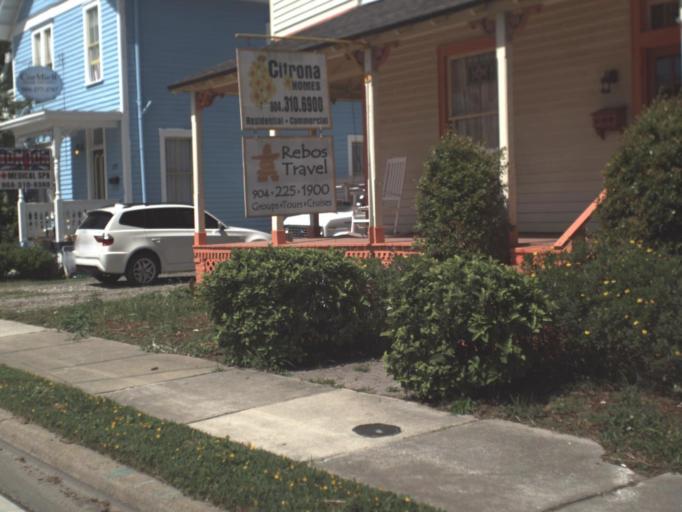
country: US
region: Florida
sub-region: Nassau County
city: Fernandina Beach
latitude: 30.6673
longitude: -81.4594
